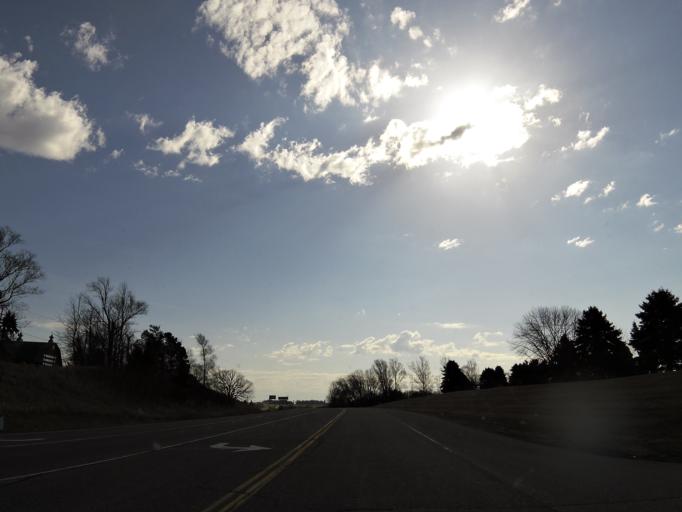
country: US
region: Minnesota
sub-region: Washington County
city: Woodbury
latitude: 44.8906
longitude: -92.8830
